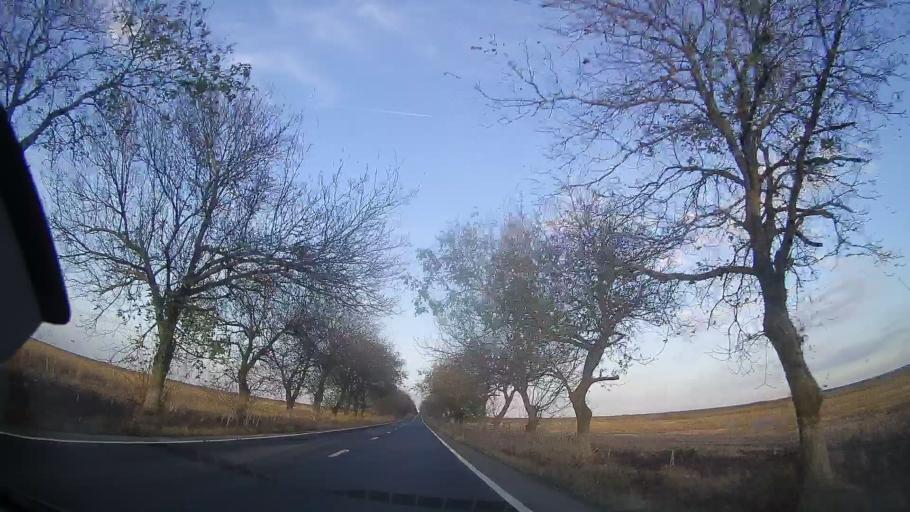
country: RO
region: Constanta
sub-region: Comuna Chirnogeni
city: Chirnogeni
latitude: 43.8515
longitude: 28.2434
